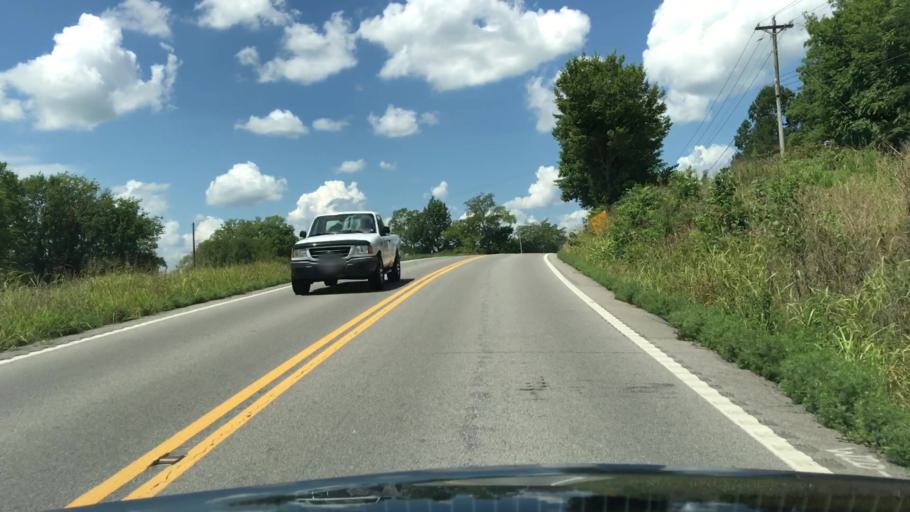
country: US
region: Tennessee
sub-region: Williamson County
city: Nolensville
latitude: 35.8518
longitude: -86.6486
